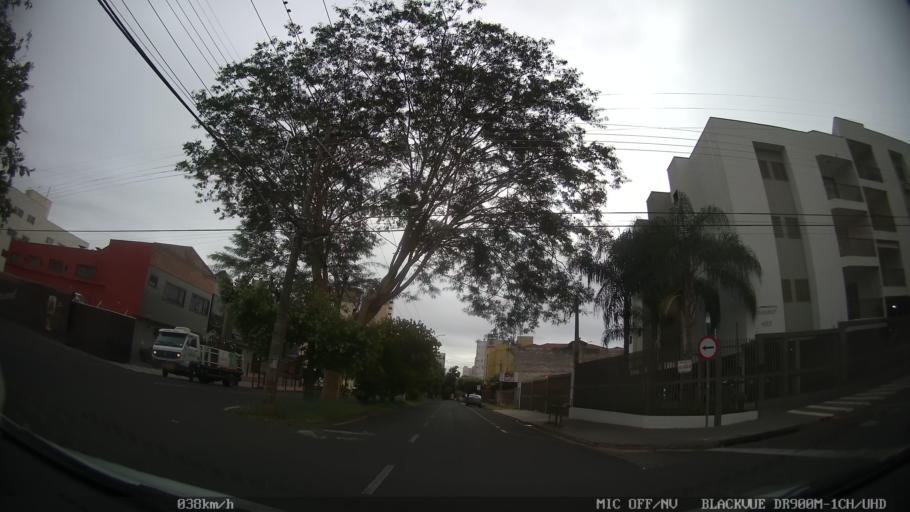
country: BR
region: Sao Paulo
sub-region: Sao Jose Do Rio Preto
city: Sao Jose do Rio Preto
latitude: -20.8333
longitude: -49.3882
